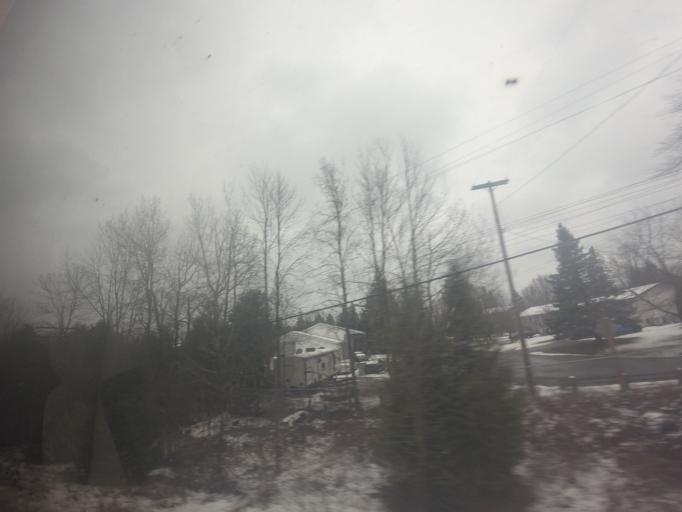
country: CA
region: Ontario
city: Cobourg
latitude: 43.9579
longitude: -78.1971
